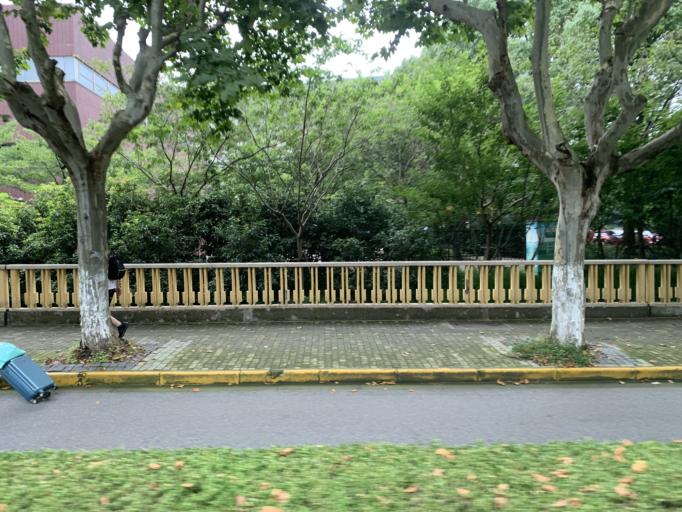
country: CN
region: Shanghai Shi
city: Huamu
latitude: 31.2190
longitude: 121.5405
